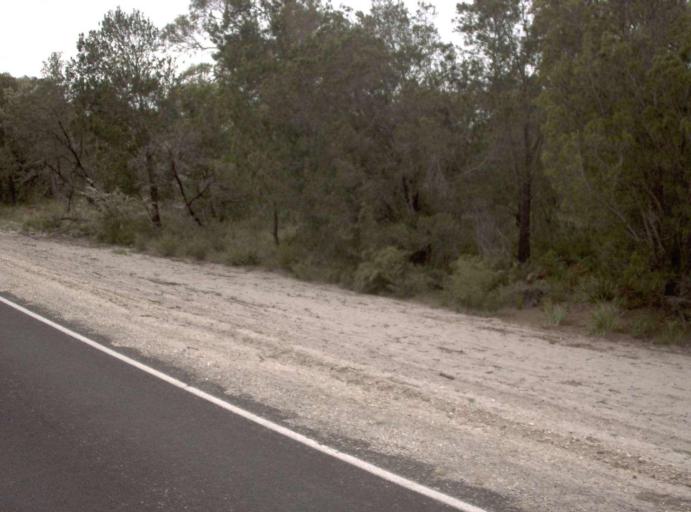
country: AU
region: Victoria
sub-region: Wellington
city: Sale
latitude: -38.1780
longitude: 147.3794
